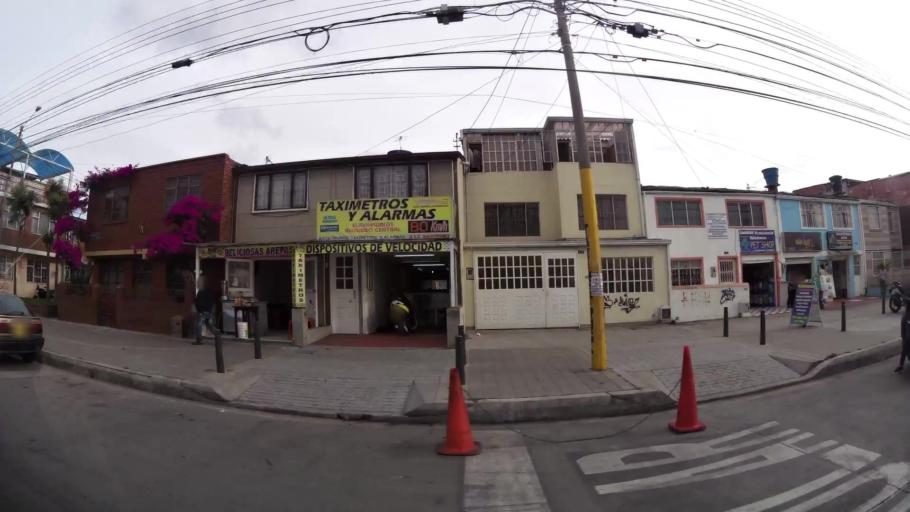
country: CO
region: Cundinamarca
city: Soacha
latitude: 4.6182
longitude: -74.1594
